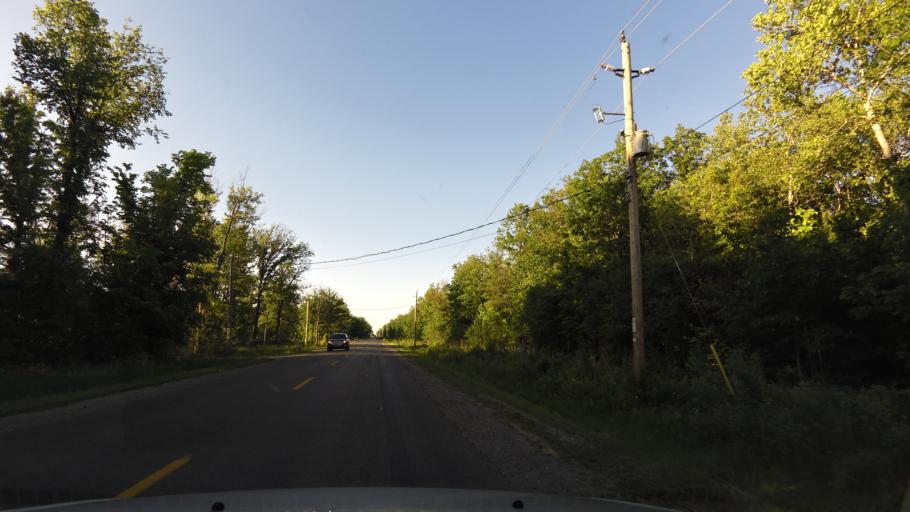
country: CA
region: Ontario
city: Ancaster
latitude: 43.0385
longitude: -80.0706
